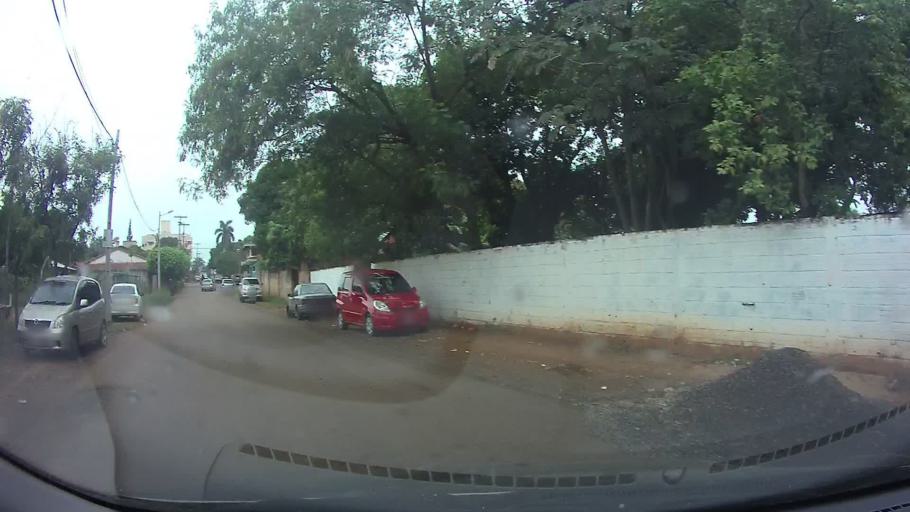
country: PY
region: Central
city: Itaugua
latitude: -25.3906
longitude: -57.3523
